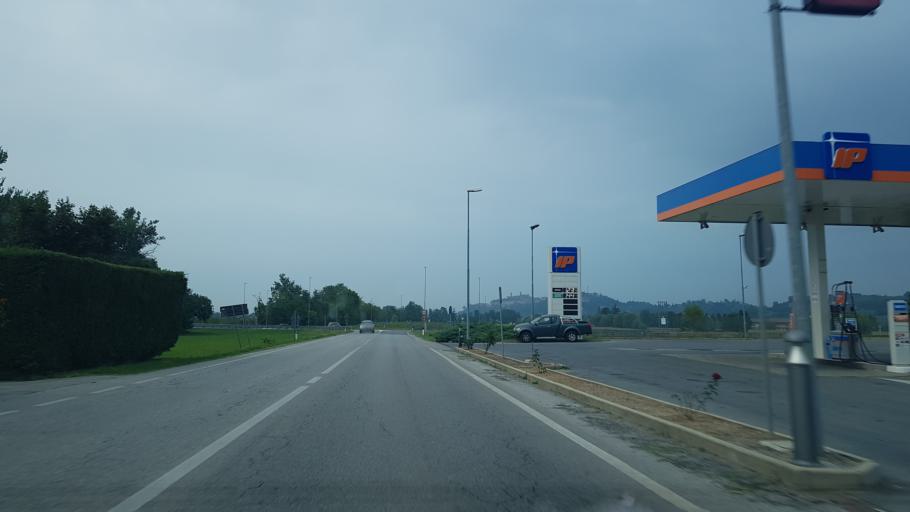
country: IT
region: Piedmont
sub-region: Provincia di Cuneo
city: Villanova Mondovi
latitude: 44.3663
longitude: 7.7968
